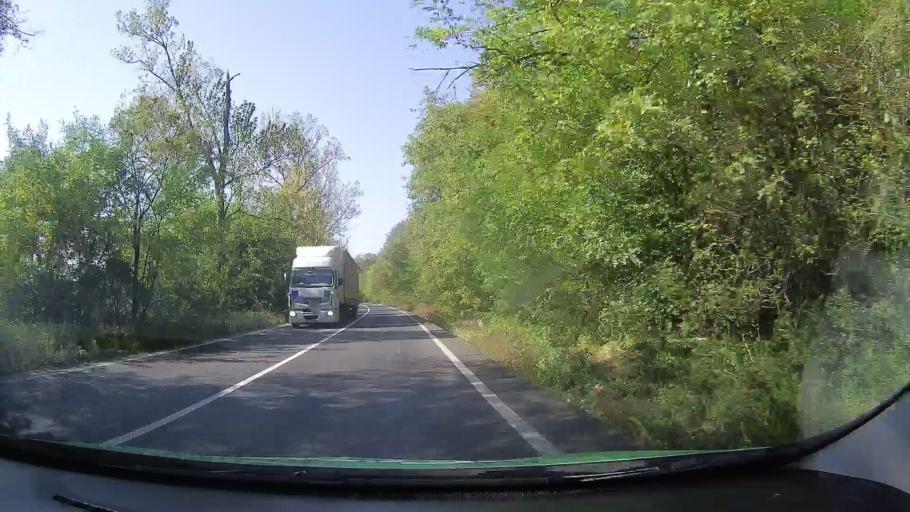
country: RO
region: Arad
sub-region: Comuna Savarsin
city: Savarsin
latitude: 46.0161
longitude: 22.2507
